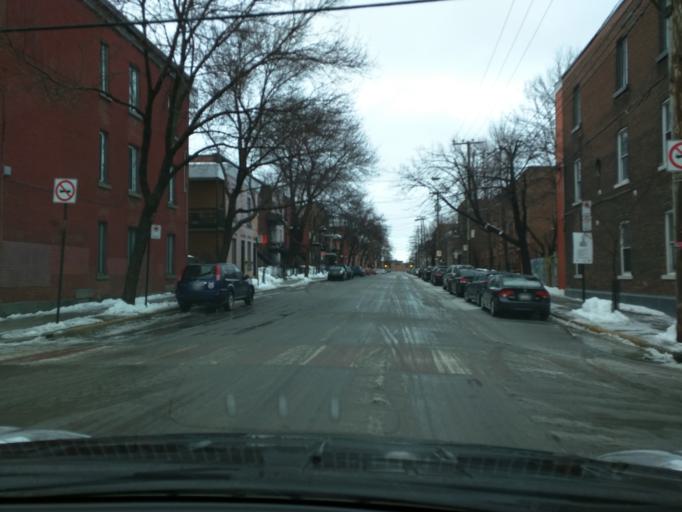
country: CA
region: Quebec
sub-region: Monteregie
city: Longueuil
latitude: 45.5285
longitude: -73.5509
